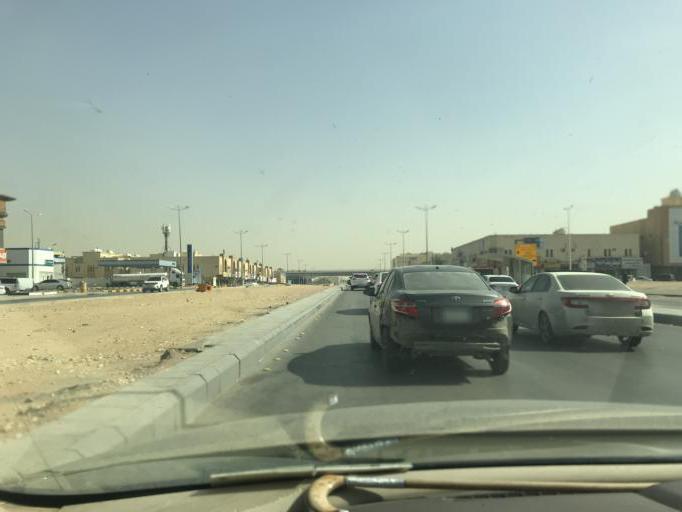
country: SA
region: Ar Riyad
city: Riyadh
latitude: 24.7965
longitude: 46.7421
